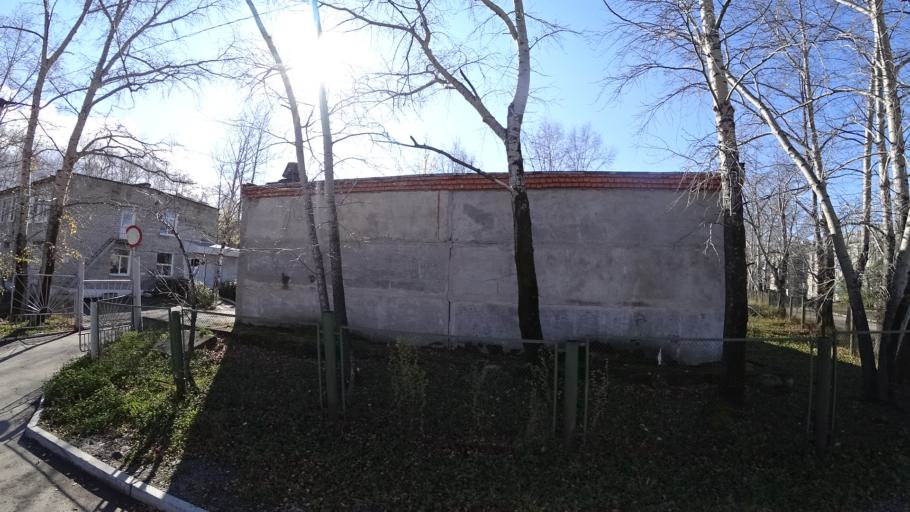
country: RU
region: Khabarovsk Krai
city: Amursk
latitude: 50.2230
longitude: 136.9075
